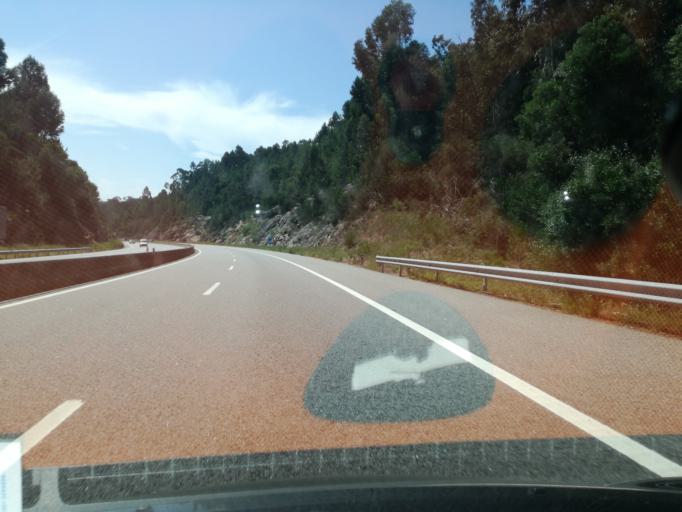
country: PT
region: Viana do Castelo
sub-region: Viana do Castelo
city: Meadela
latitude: 41.7493
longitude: -8.7998
